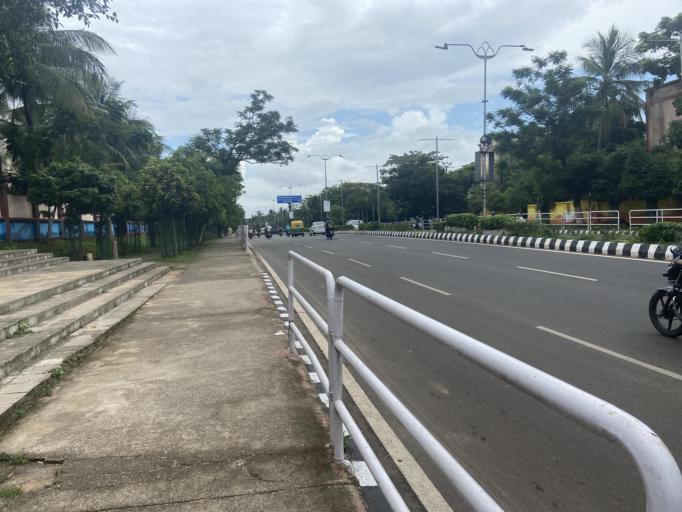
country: IN
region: Odisha
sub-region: Khordha
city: Bhubaneshwar
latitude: 20.2902
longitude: 85.8260
